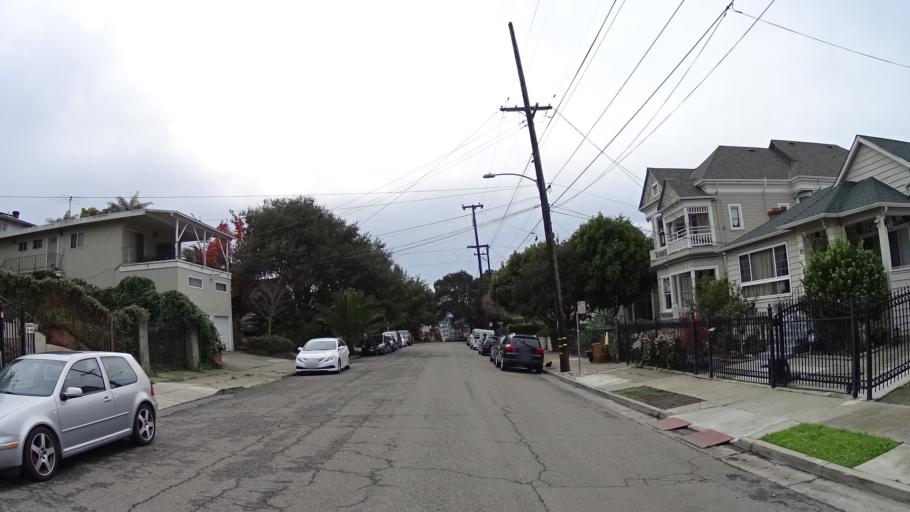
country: US
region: California
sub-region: Alameda County
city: Alameda
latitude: 37.7951
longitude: -122.2418
